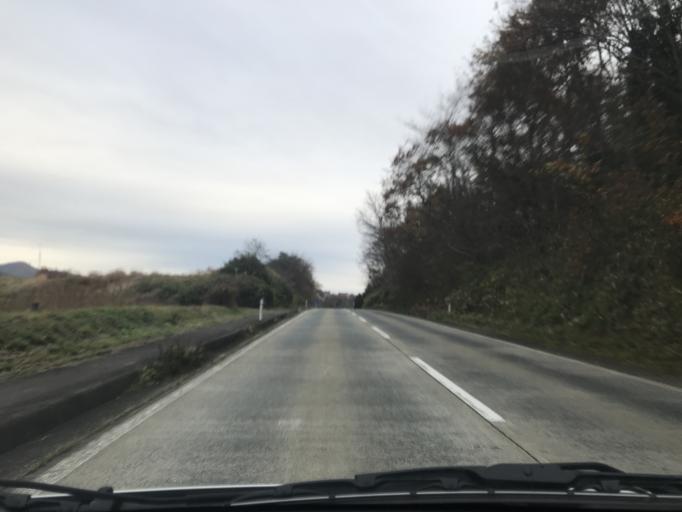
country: JP
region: Iwate
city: Kitakami
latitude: 39.2895
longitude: 141.2157
